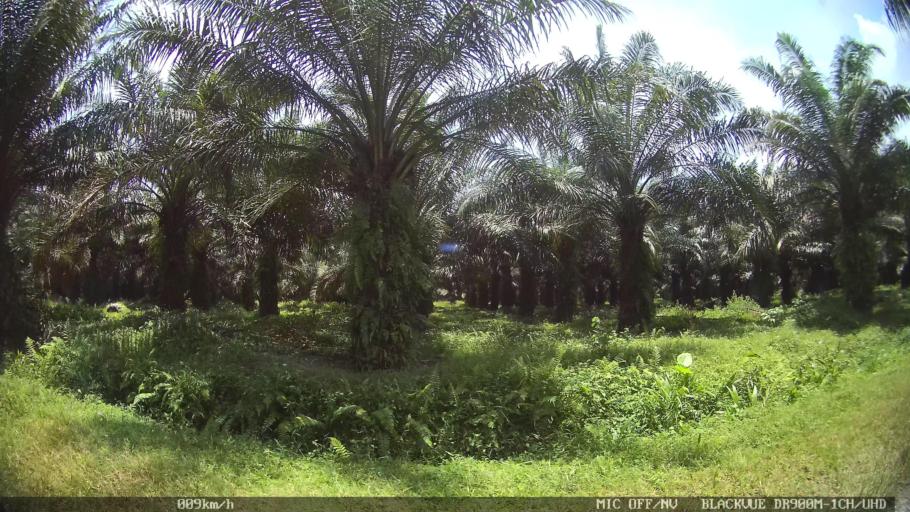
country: ID
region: North Sumatra
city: Percut
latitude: 3.5388
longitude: 98.8712
